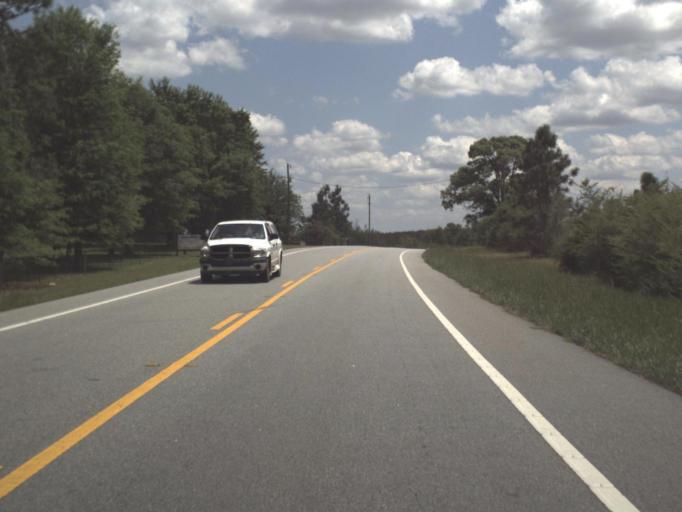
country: US
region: Florida
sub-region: Escambia County
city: Molino
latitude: 30.8135
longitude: -87.4280
